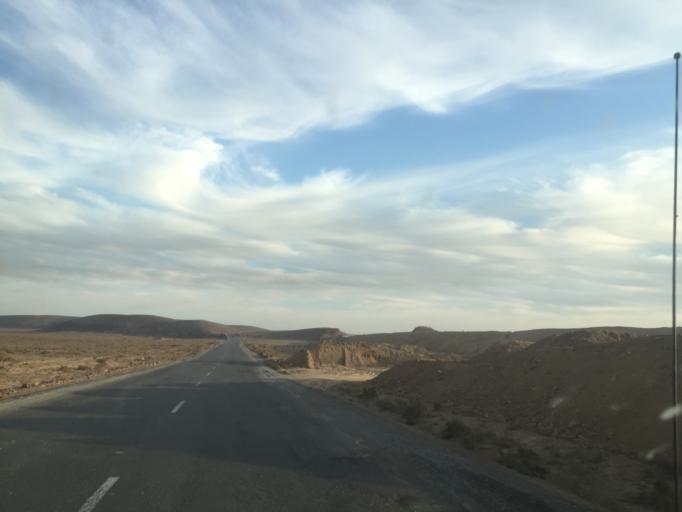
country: KZ
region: Almaty Oblysy
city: Ulken
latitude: 45.0668
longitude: 73.9978
